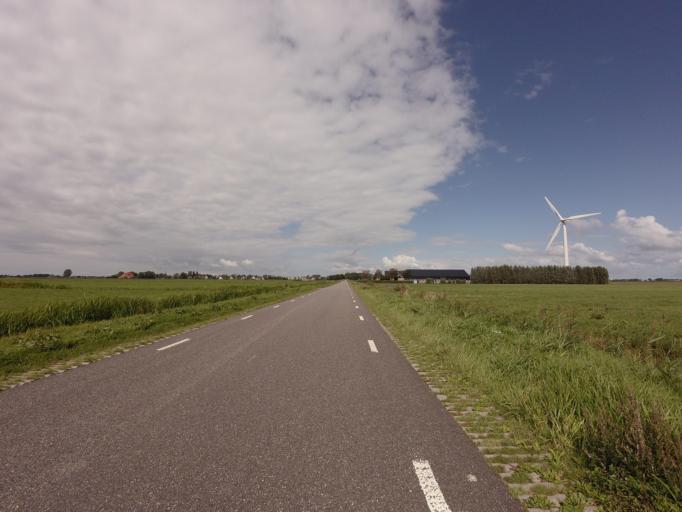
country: NL
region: Friesland
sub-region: Sudwest Fryslan
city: IJlst
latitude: 53.0001
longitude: 5.6358
